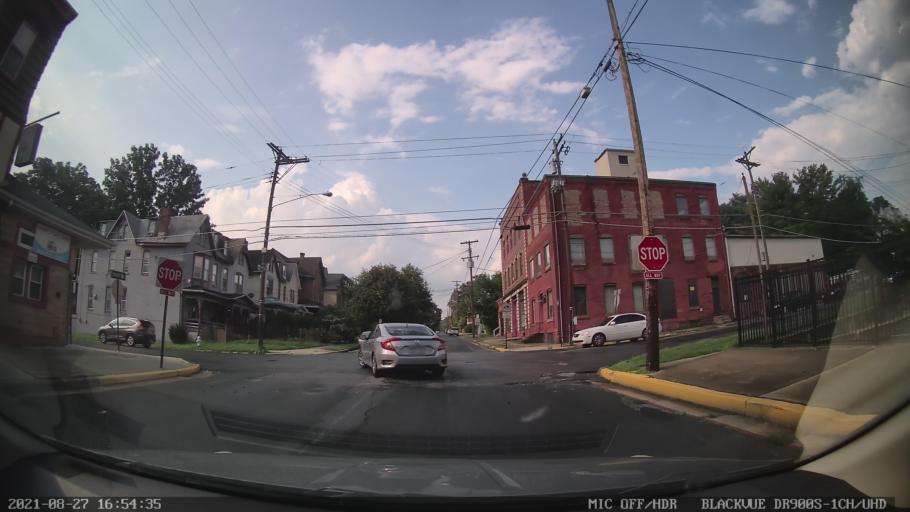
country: US
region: Pennsylvania
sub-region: Berks County
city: Reading
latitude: 40.3444
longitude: -75.9315
